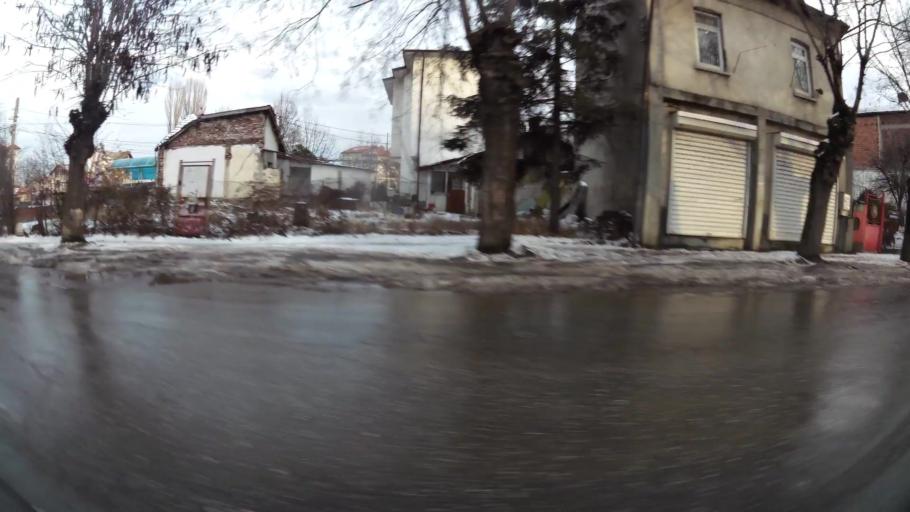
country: BG
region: Sofia-Capital
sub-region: Stolichna Obshtina
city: Sofia
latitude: 42.7223
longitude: 23.3425
